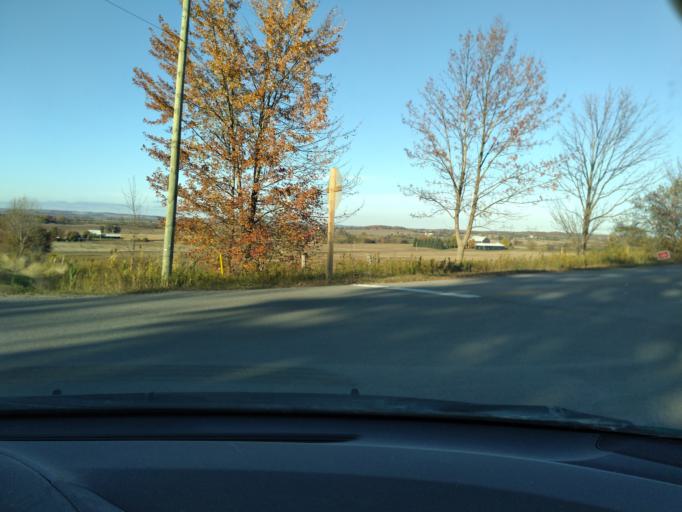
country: CA
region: Ontario
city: Bradford West Gwillimbury
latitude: 44.0752
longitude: -79.7414
